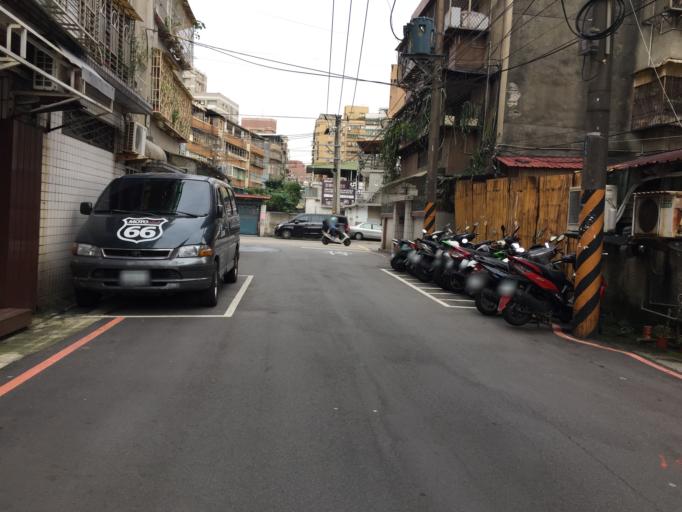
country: TW
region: Taipei
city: Taipei
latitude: 25.0094
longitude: 121.5186
